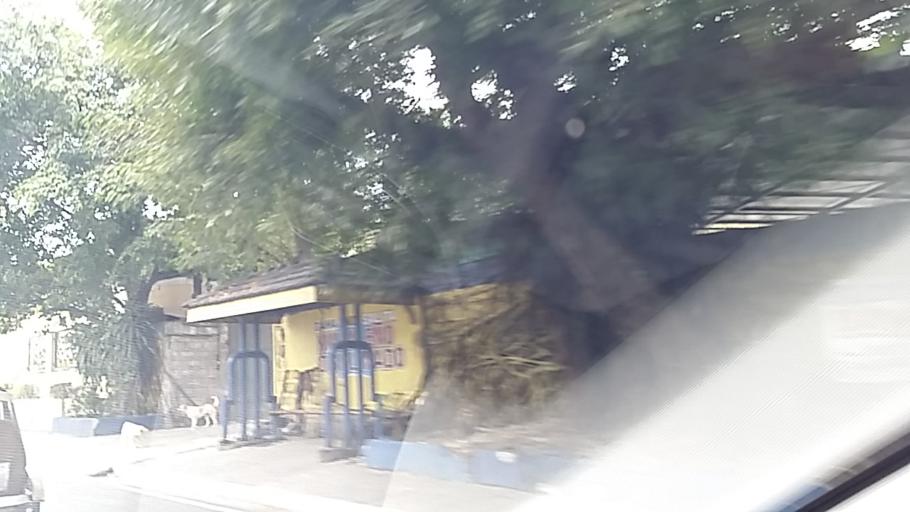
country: PH
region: Metro Manila
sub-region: Mandaluyong
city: Mandaluyong City
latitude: 14.5794
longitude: 121.0442
